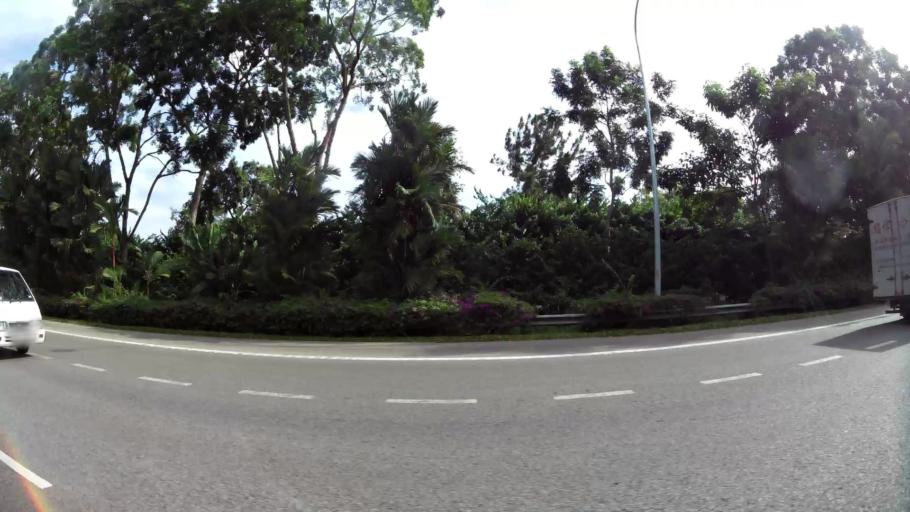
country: MY
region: Johor
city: Johor Bahru
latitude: 1.3321
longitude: 103.6540
